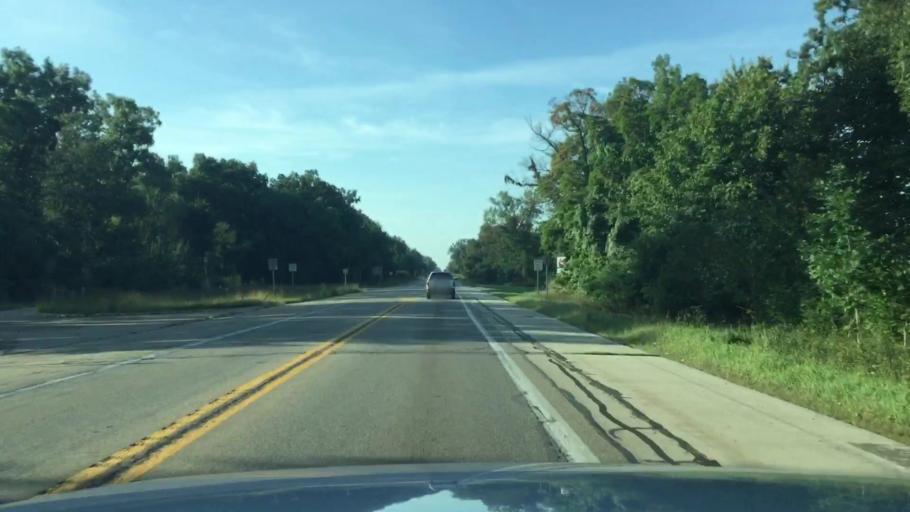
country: US
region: Michigan
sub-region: Jackson County
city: Vandercook Lake
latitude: 42.1150
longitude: -84.3641
